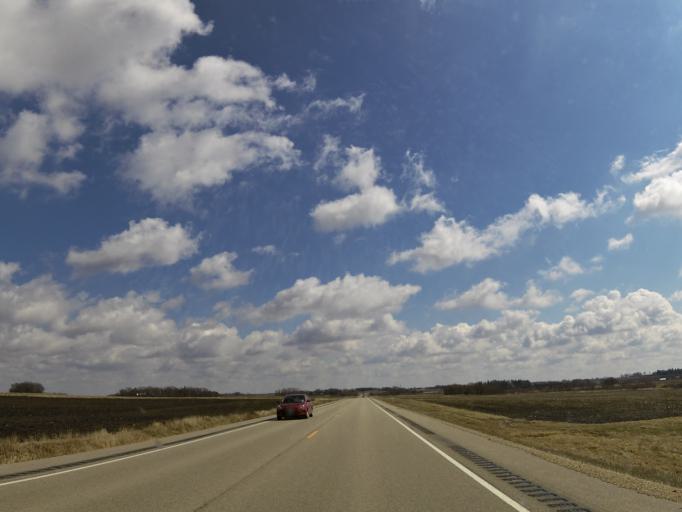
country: US
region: Minnesota
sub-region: Goodhue County
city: Kenyon
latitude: 44.1892
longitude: -92.9174
